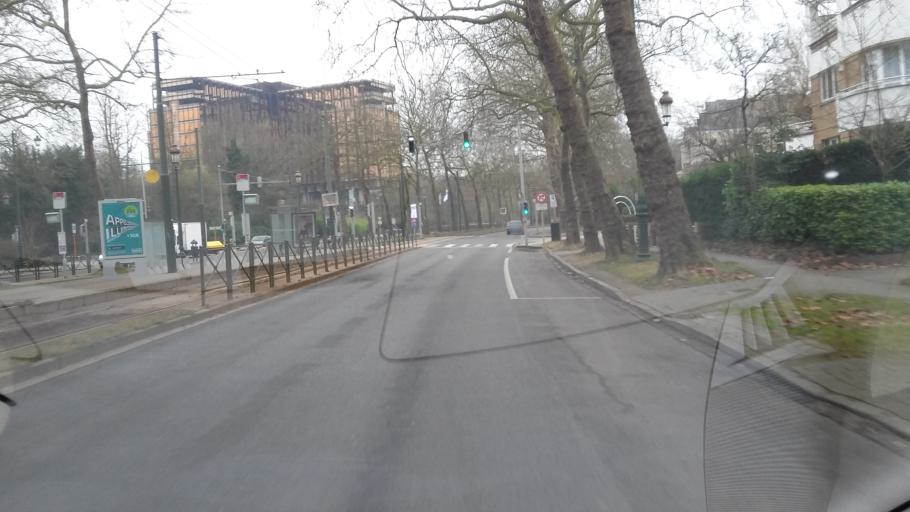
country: BE
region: Flanders
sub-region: Provincie Vlaams-Brabant
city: Hoeilaart
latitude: 50.8056
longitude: 4.4266
